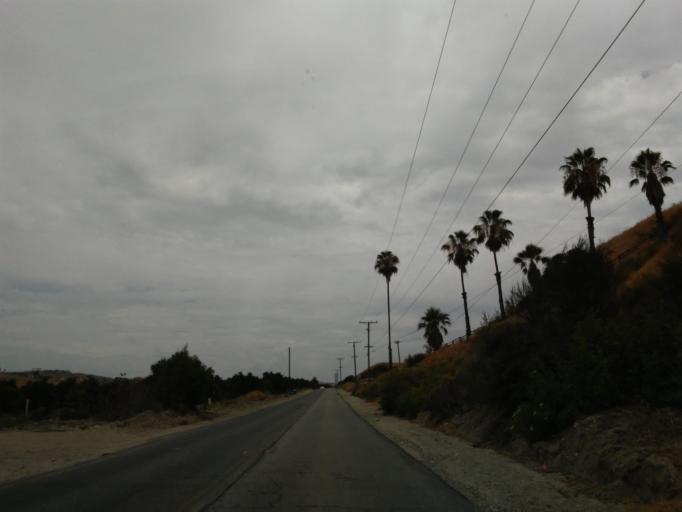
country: US
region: California
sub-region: San Bernardino County
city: Redlands
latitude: 34.0223
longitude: -117.1955
